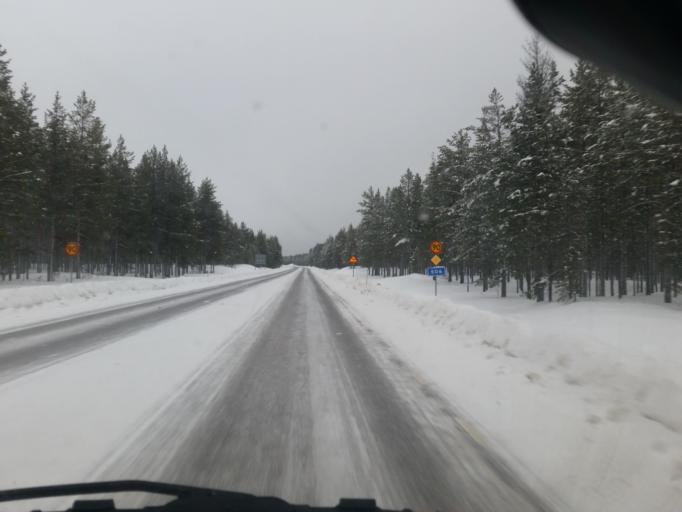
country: SE
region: Norrbotten
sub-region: Pitea Kommun
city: Pitea
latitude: 65.2381
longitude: 21.5271
